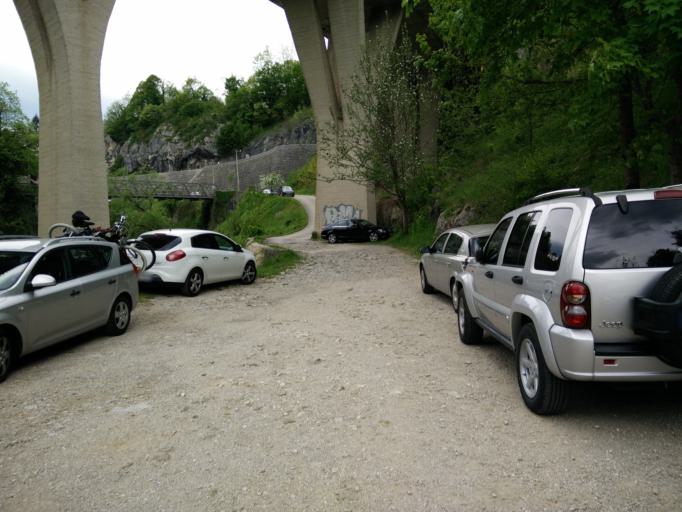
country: HR
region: Karlovacka
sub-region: Grad Karlovac
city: Slunj
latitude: 45.1217
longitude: 15.5889
